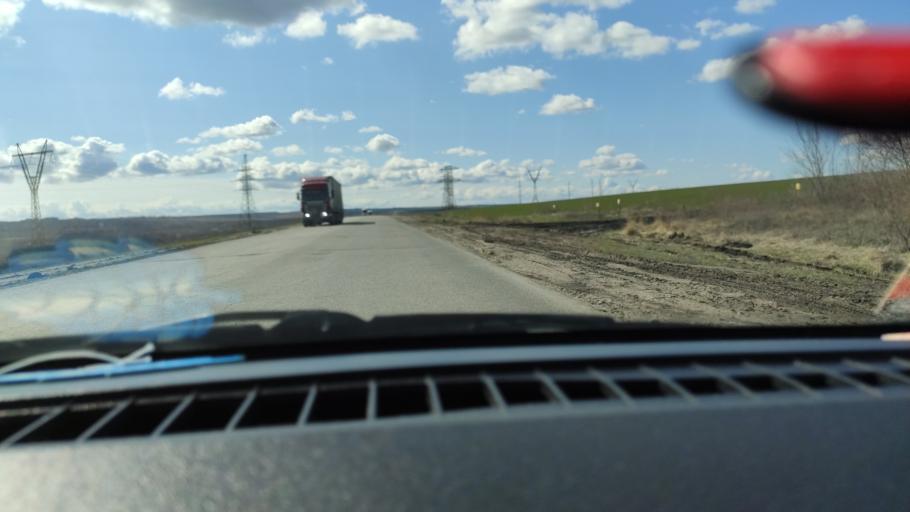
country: RU
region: Samara
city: Varlamovo
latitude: 53.0810
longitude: 48.3543
